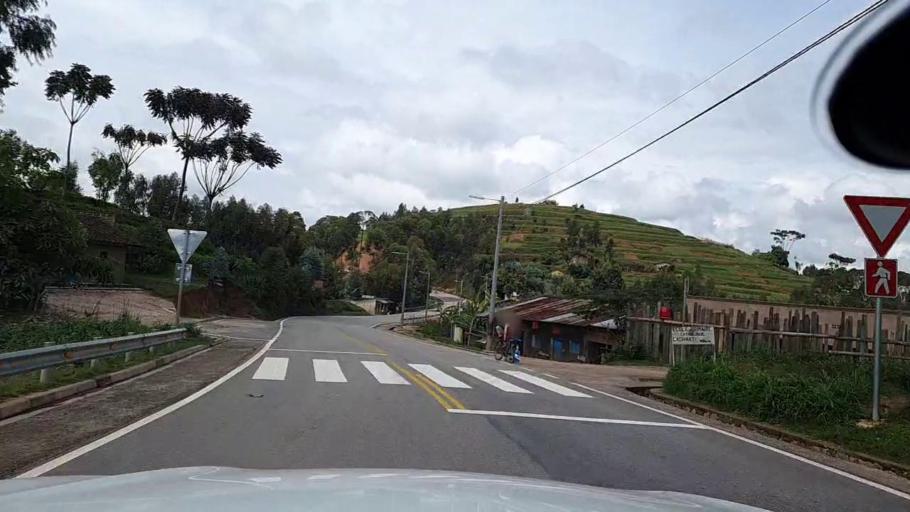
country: RW
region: Southern Province
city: Nzega
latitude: -2.5198
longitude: 29.4574
